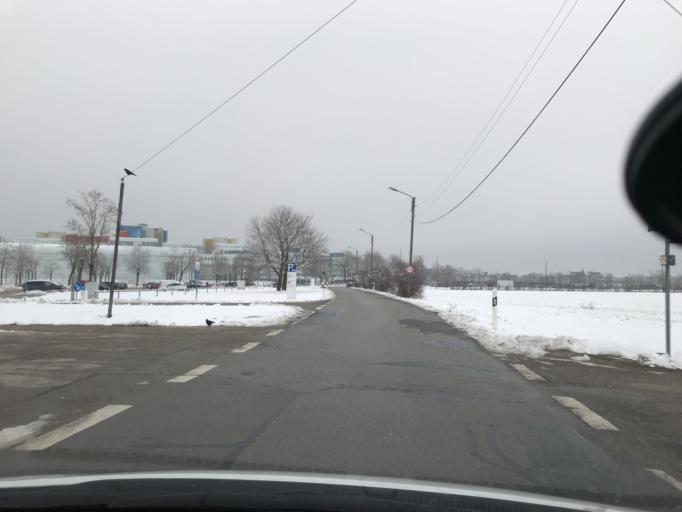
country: DE
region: Bavaria
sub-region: Upper Bavaria
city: Neubiberg
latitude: 48.0856
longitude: 11.6496
